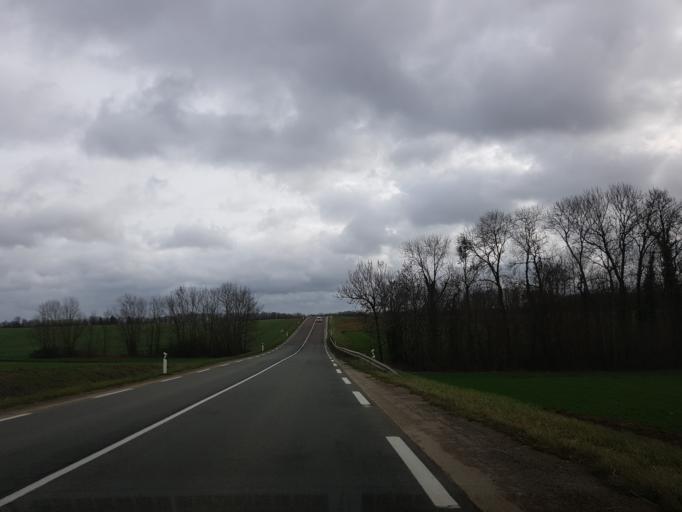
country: FR
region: Champagne-Ardenne
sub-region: Departement de la Haute-Marne
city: Chalindrey
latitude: 47.8422
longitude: 5.4643
